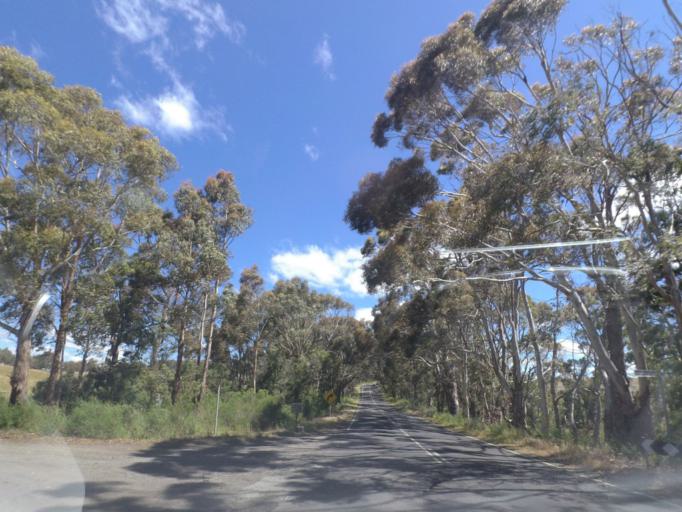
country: AU
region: Victoria
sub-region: Mount Alexander
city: Castlemaine
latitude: -37.3062
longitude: 144.4142
